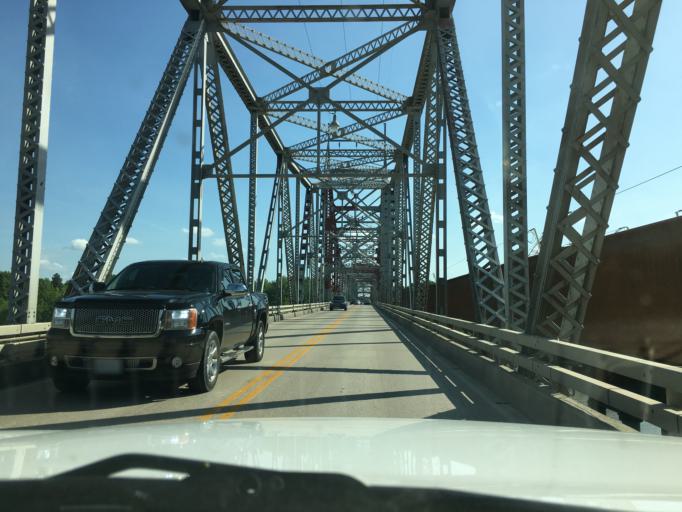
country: US
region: Missouri
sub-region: Franklin County
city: Washington
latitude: 38.5582
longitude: -90.9978
